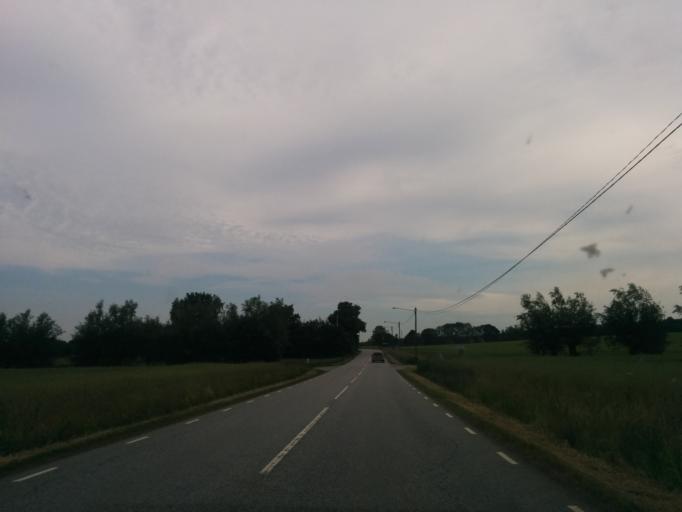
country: SE
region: Skane
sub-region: Lunds Kommun
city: Genarp
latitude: 55.6102
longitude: 13.4055
